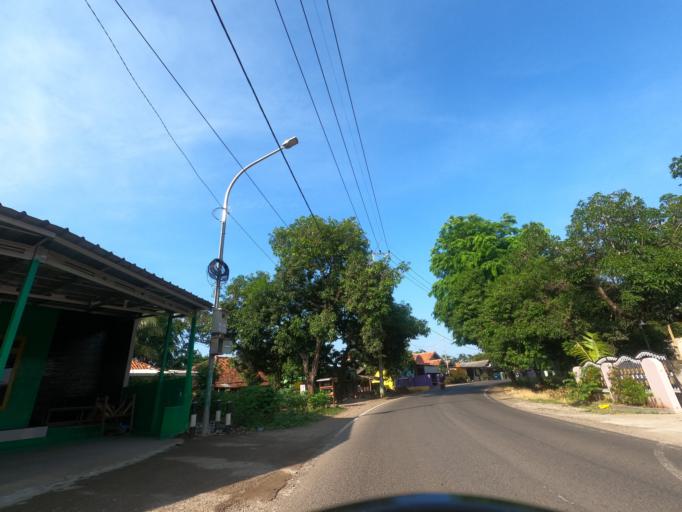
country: ID
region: West Java
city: Pamanukan
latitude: -6.5546
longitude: 107.8264
